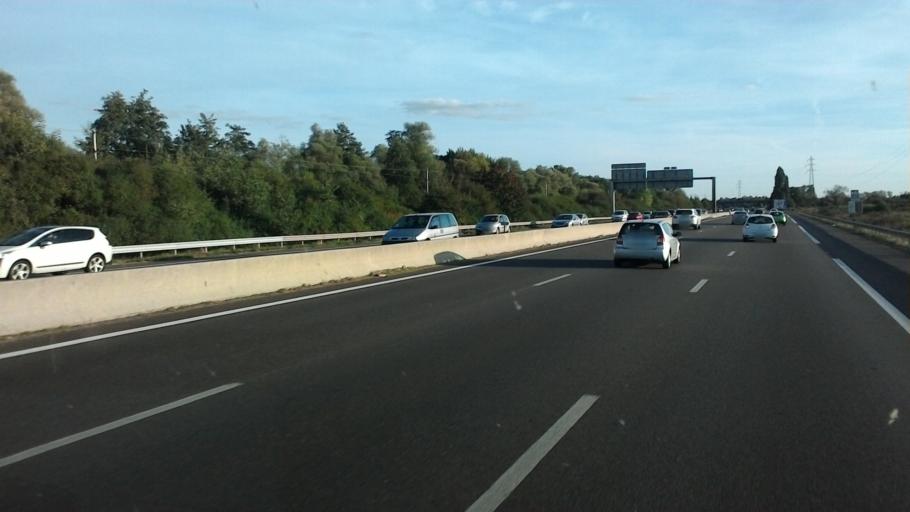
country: FR
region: Lorraine
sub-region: Departement de la Moselle
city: Maizieres-les-Metz
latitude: 49.1887
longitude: 6.1760
